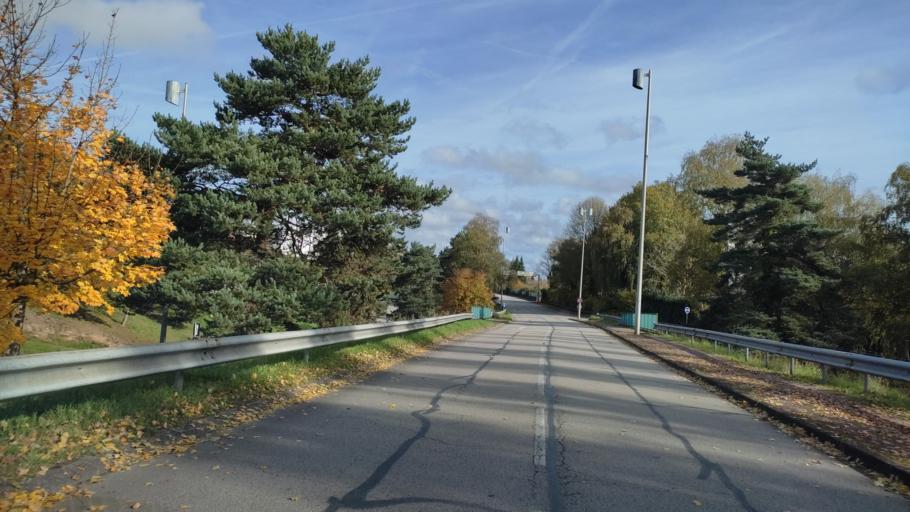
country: FR
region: Limousin
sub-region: Departement de la Haute-Vienne
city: Isle
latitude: 45.8148
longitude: 1.2316
